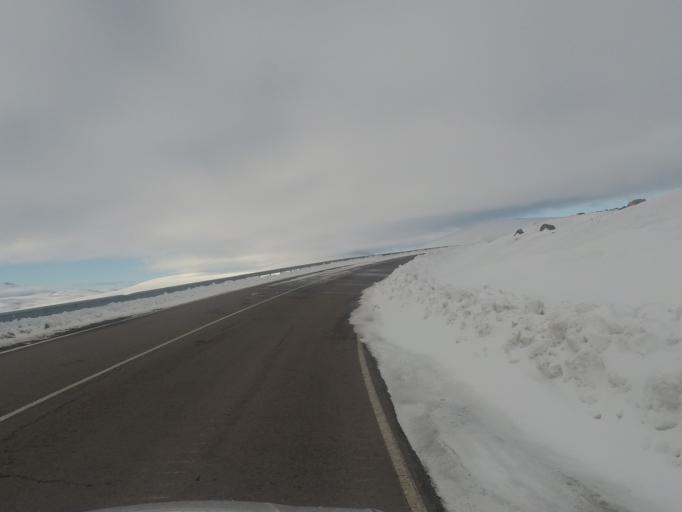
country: GE
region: Kvemo Kartli
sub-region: Tsalka
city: Tsalka
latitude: 41.4447
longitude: 43.8466
